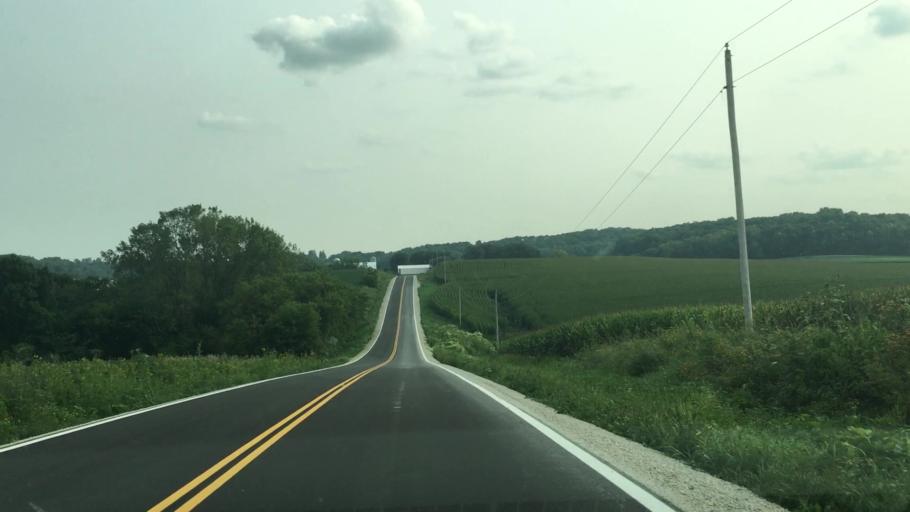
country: US
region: Minnesota
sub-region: Fillmore County
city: Preston
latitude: 43.7509
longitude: -92.0200
